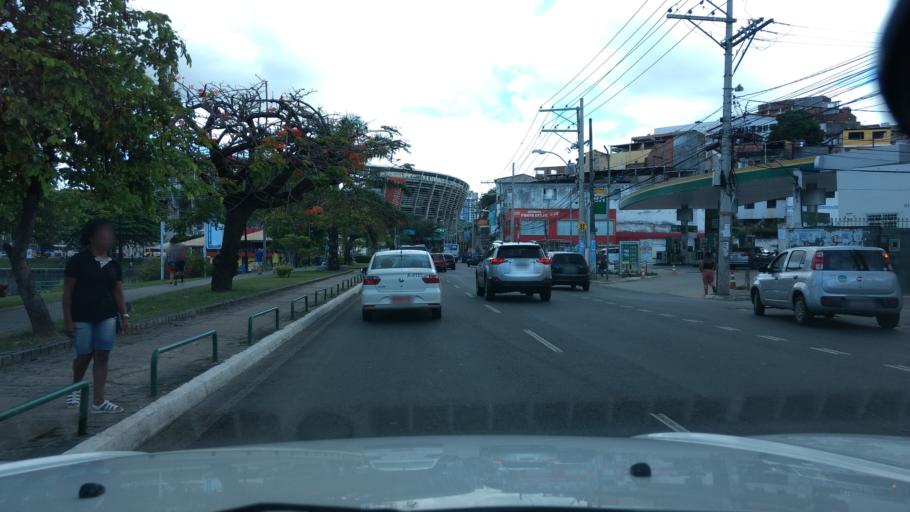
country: BR
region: Bahia
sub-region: Salvador
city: Salvador
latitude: -12.9829
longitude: -38.5038
